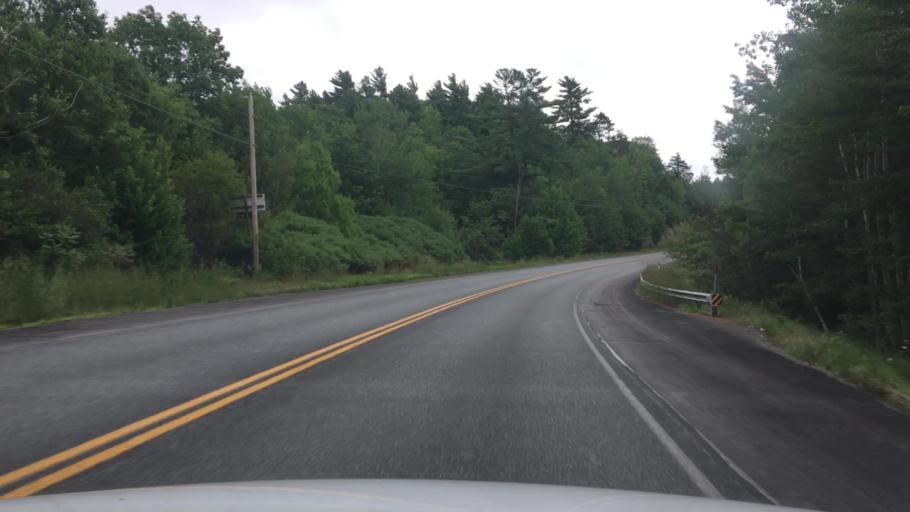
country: US
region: Maine
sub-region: Penobscot County
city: Bradley
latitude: 44.8191
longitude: -68.5048
